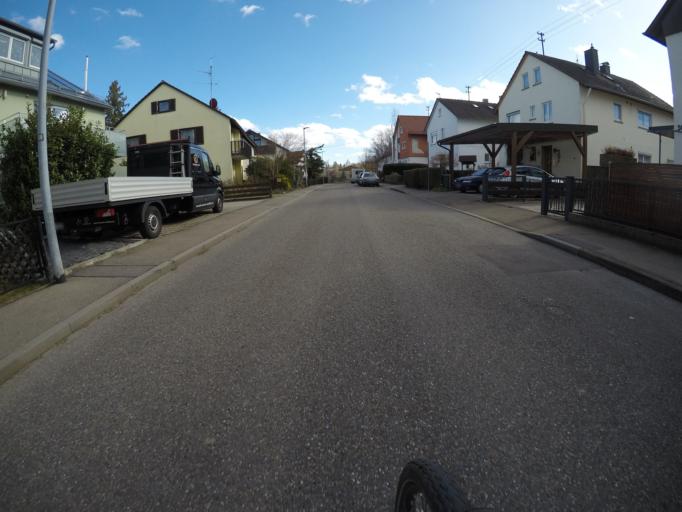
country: DE
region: Baden-Wuerttemberg
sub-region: Regierungsbezirk Stuttgart
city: Leinfelden-Echterdingen
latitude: 48.6641
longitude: 9.1746
